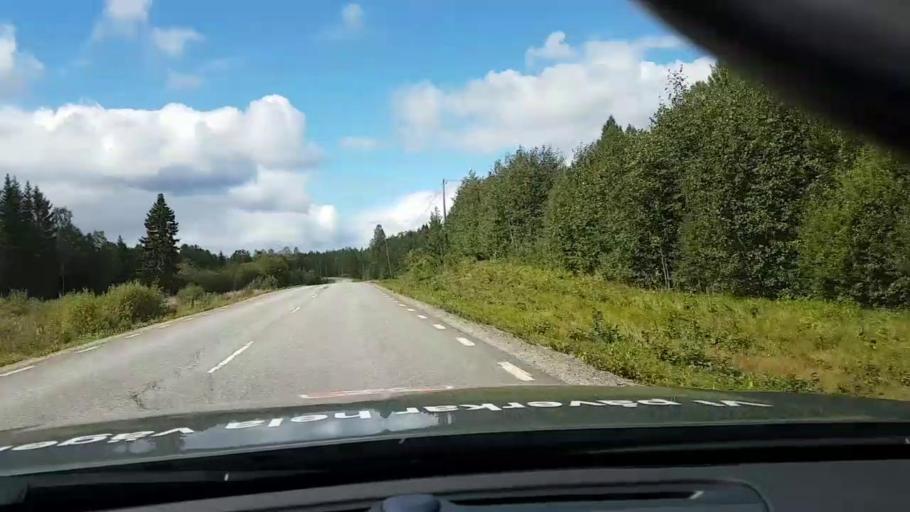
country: SE
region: Vaesternorrland
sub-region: OErnskoeldsviks Kommun
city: Bredbyn
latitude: 63.5283
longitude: 17.9921
